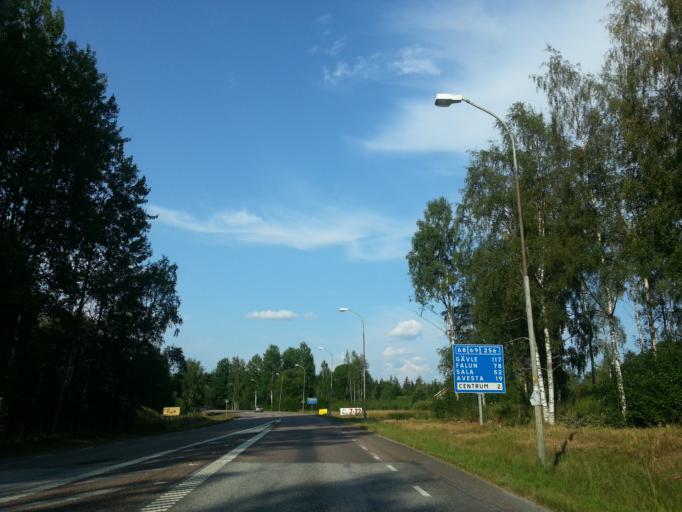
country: SE
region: Vaestmanland
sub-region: Norbergs Kommun
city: Norberg
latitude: 60.0652
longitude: 15.9121
